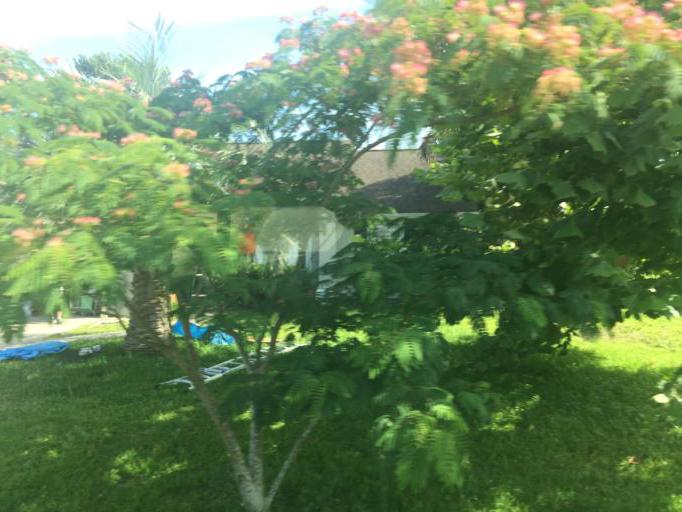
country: US
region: Florida
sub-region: Bay County
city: Laguna Beach
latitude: 30.2606
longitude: -85.9589
